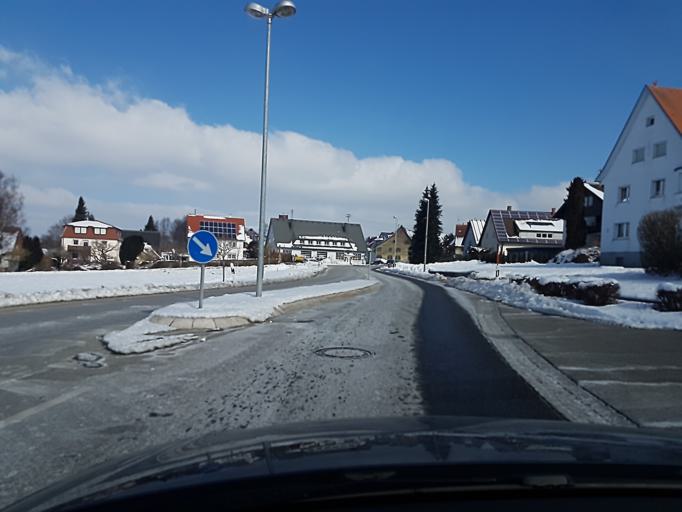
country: DE
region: Baden-Wuerttemberg
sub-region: Freiburg Region
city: Oberndorf
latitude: 48.3085
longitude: 8.5302
